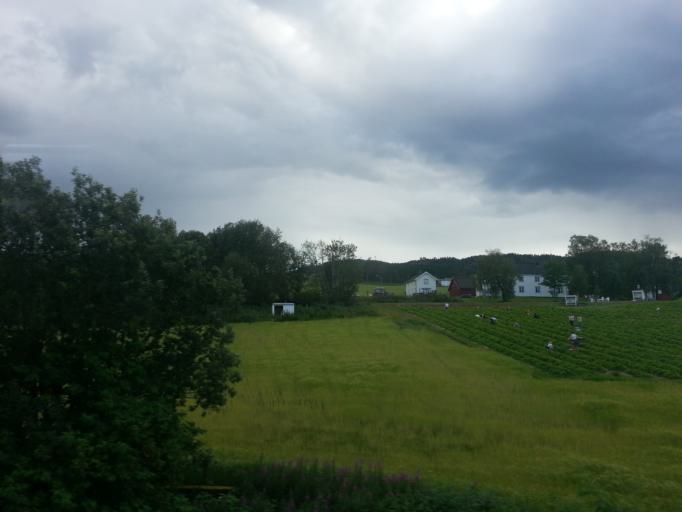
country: NO
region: Sor-Trondelag
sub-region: Malvik
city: Malvik
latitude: 63.4366
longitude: 10.6813
